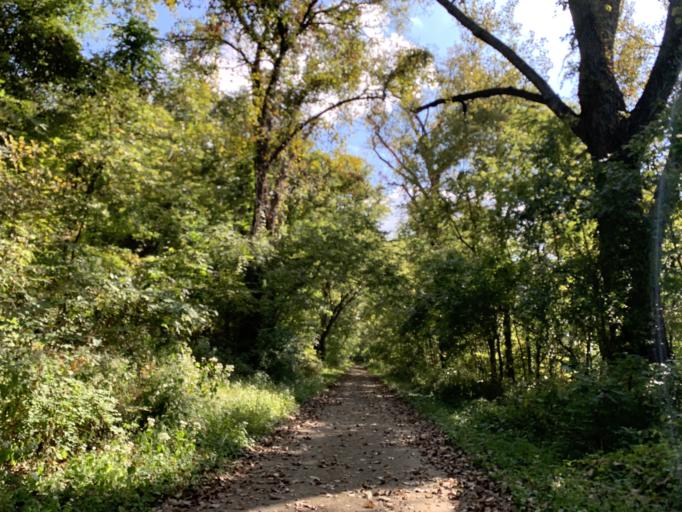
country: US
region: Indiana
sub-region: Floyd County
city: New Albany
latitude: 38.2567
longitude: -85.8323
